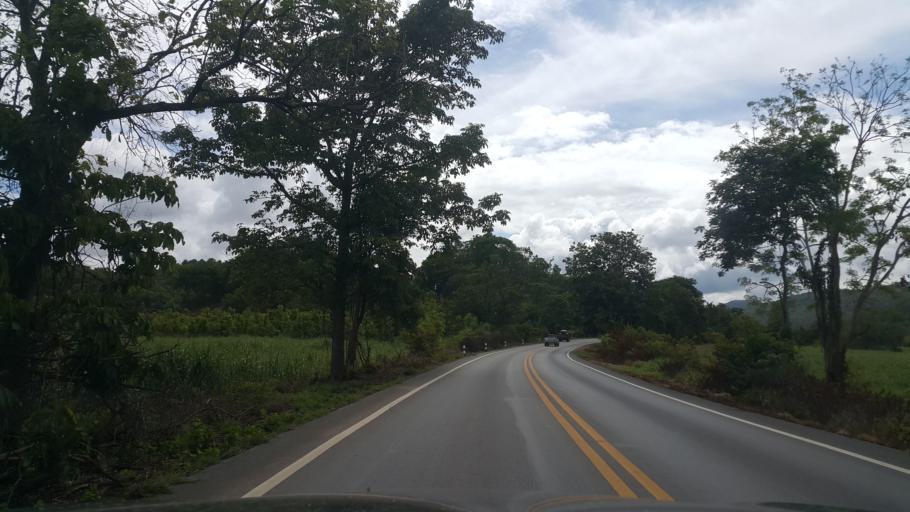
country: TH
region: Uttaradit
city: Thong Saen Khan
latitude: 17.3789
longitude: 100.2725
